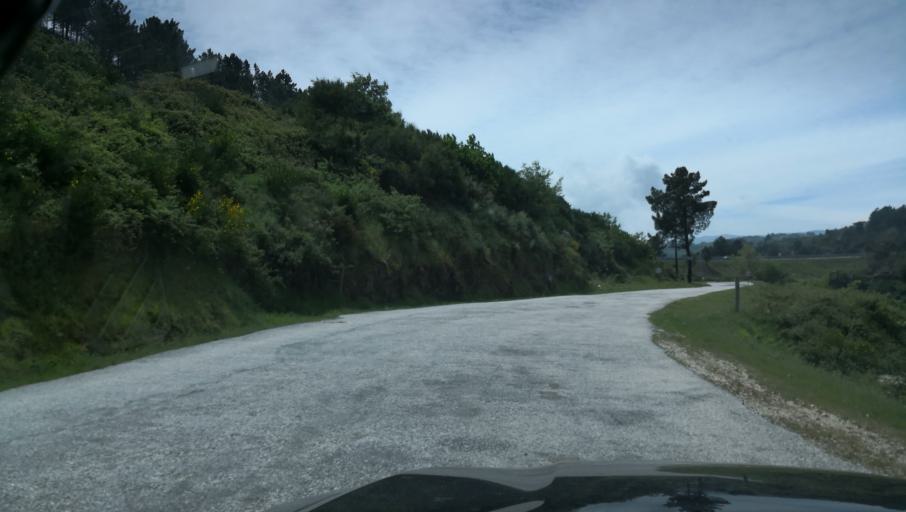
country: PT
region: Vila Real
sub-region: Vila Real
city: Vila Real
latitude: 41.2744
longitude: -7.7886
